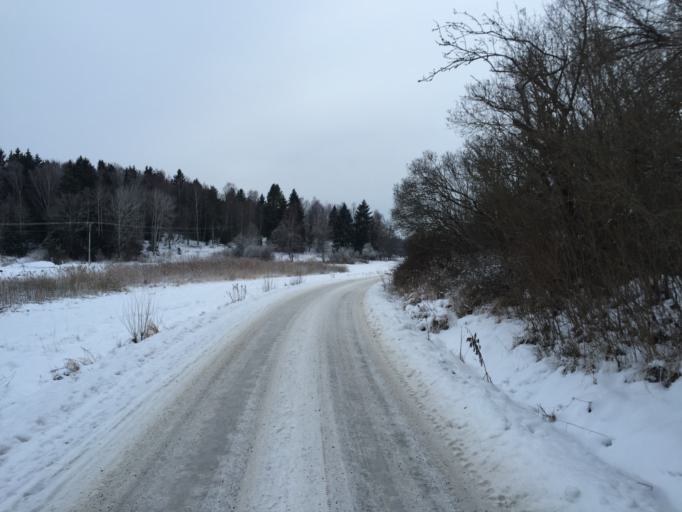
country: SE
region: Stockholm
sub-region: Salems Kommun
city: Ronninge
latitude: 59.2261
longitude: 17.7271
